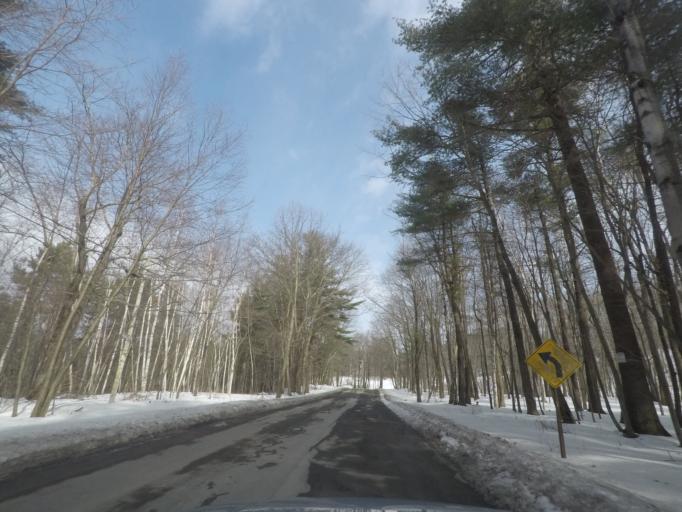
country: US
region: New York
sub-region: Saratoga County
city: Waterford
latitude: 42.7771
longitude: -73.6002
